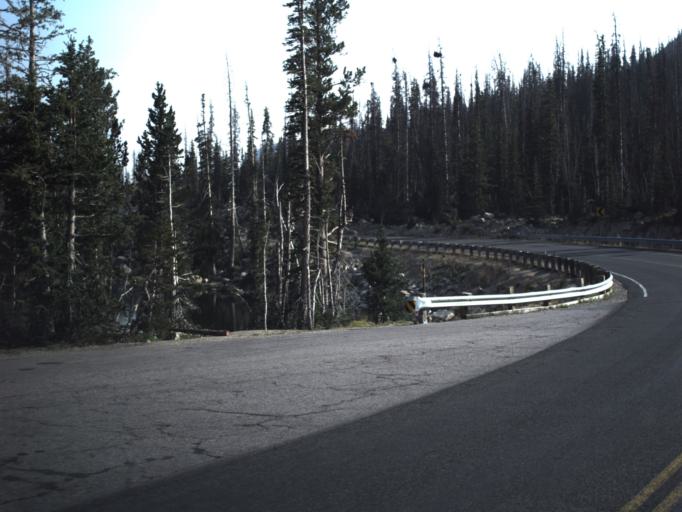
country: US
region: Utah
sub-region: Summit County
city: Kamas
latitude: 40.7123
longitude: -110.8947
